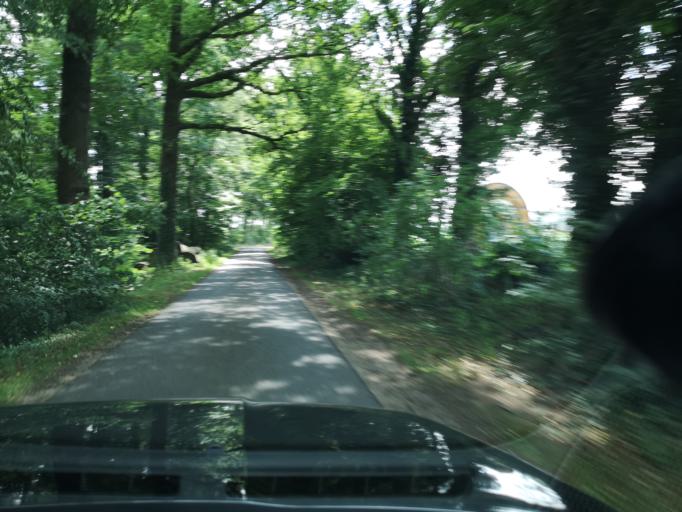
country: DE
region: North Rhine-Westphalia
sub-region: Regierungsbezirk Munster
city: Rhede
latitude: 51.8164
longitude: 6.6832
